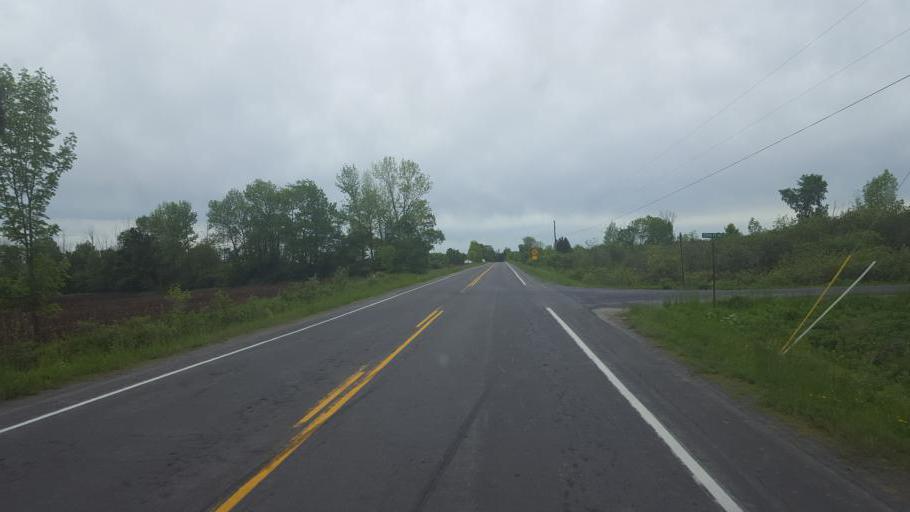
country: US
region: New York
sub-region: Herkimer County
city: Ilion
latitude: 42.9315
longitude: -75.0688
